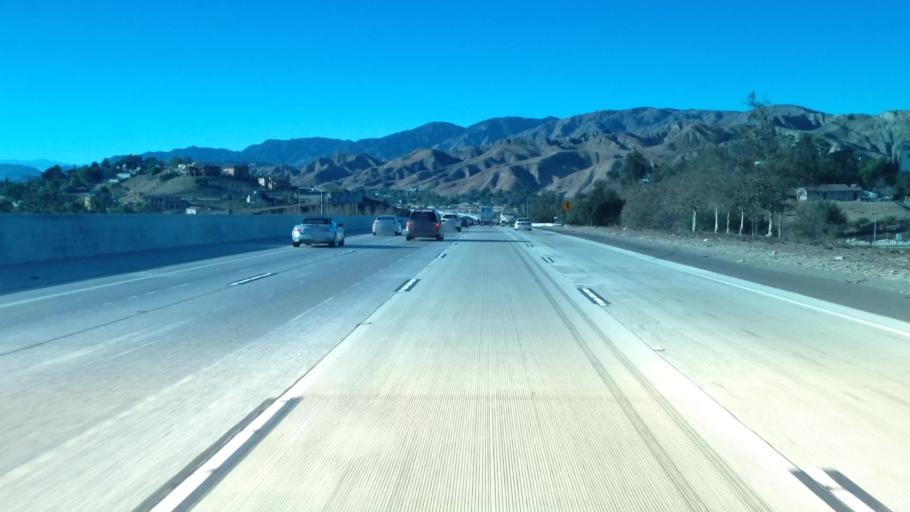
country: US
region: California
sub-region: Los Angeles County
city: Burbank
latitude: 34.2585
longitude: -118.3283
